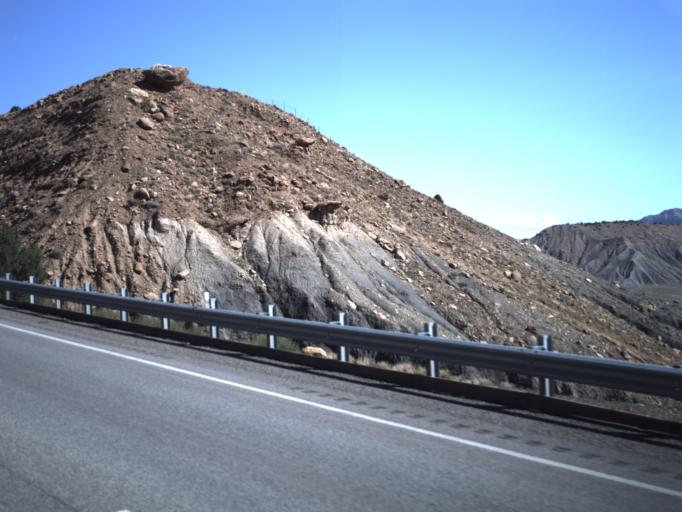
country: US
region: Utah
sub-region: Carbon County
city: East Carbon City
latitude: 39.3950
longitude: -110.4184
